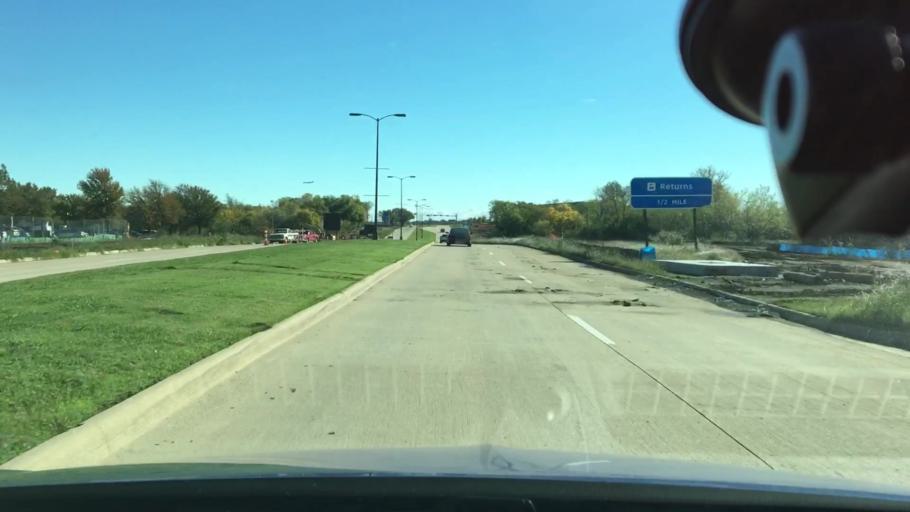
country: US
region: Texas
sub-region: Tarrant County
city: Euless
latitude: 32.8528
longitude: -97.0372
